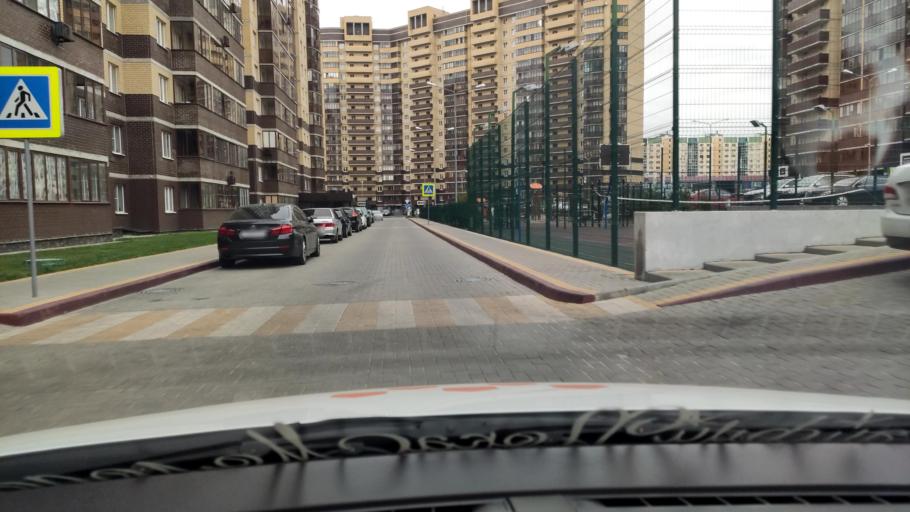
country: RU
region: Voronezj
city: Voronezh
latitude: 51.7162
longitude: 39.1939
